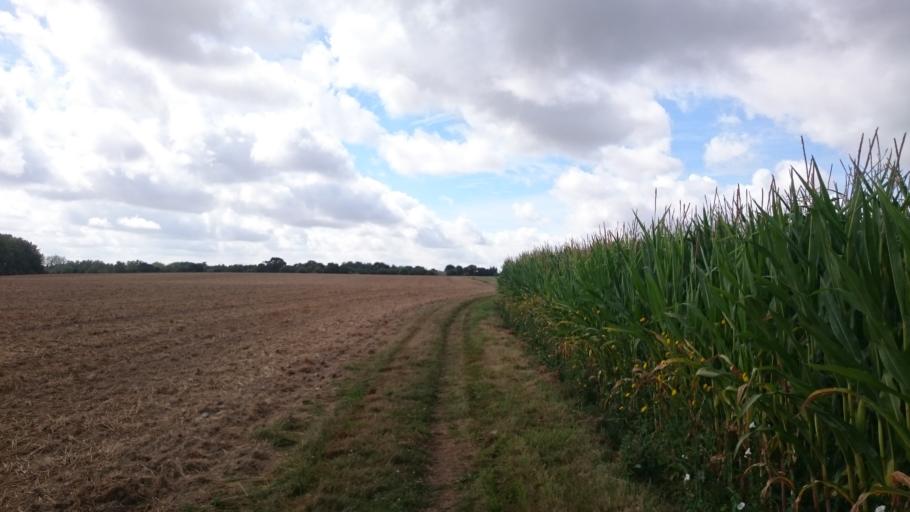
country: FR
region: Brittany
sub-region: Departement d'Ille-et-Vilaine
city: Vern-sur-Seiche
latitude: 48.0393
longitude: -1.6153
